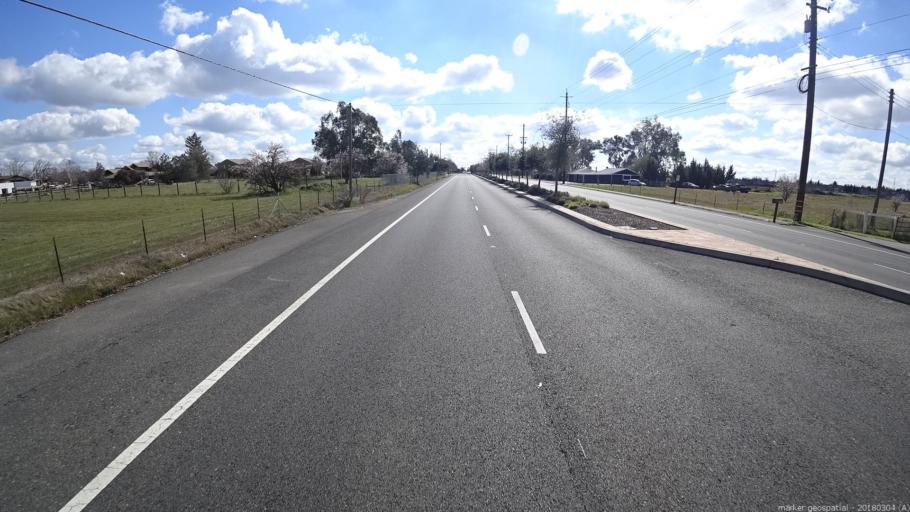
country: US
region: California
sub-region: Sacramento County
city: Vineyard
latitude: 38.4684
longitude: -121.3347
